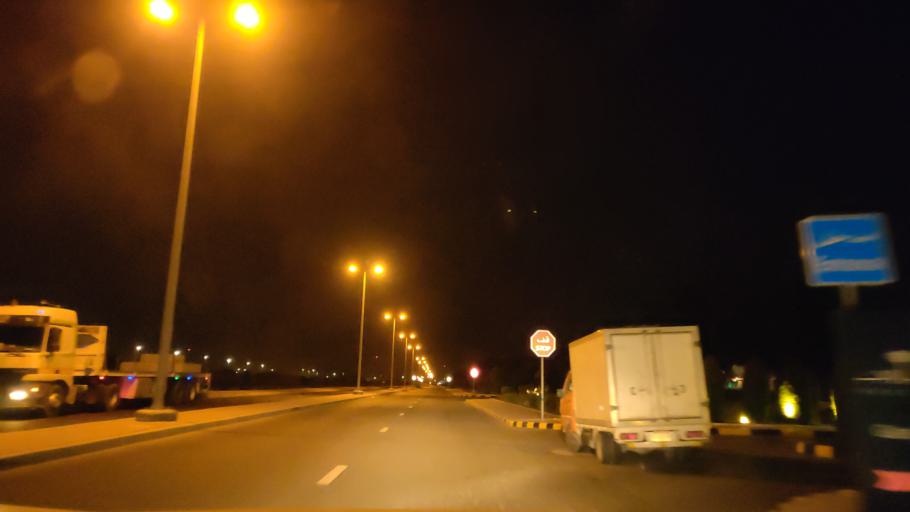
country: KW
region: Mubarak al Kabir
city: Sabah as Salim
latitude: 29.2623
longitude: 48.0223
